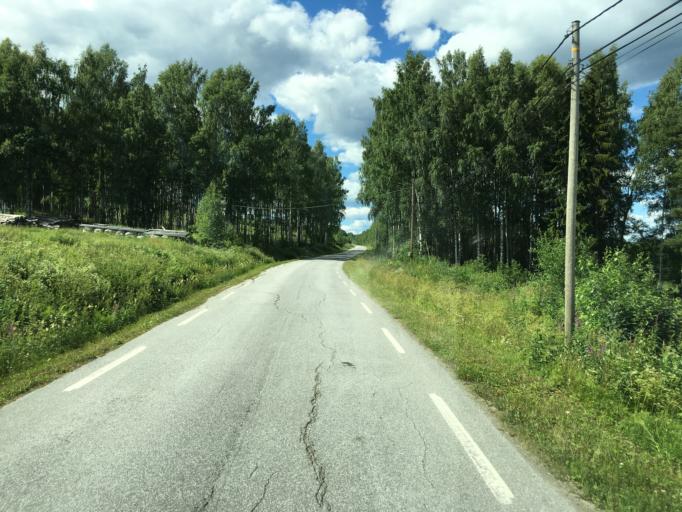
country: NO
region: Oppland
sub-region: Sondre Land
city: Hov
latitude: 60.6884
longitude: 10.3025
